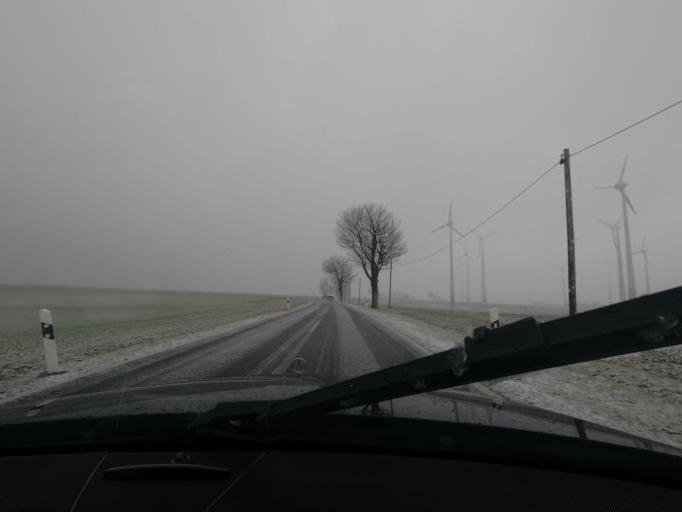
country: DE
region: Thuringia
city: Buttstedt
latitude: 51.2347
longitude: 10.2910
